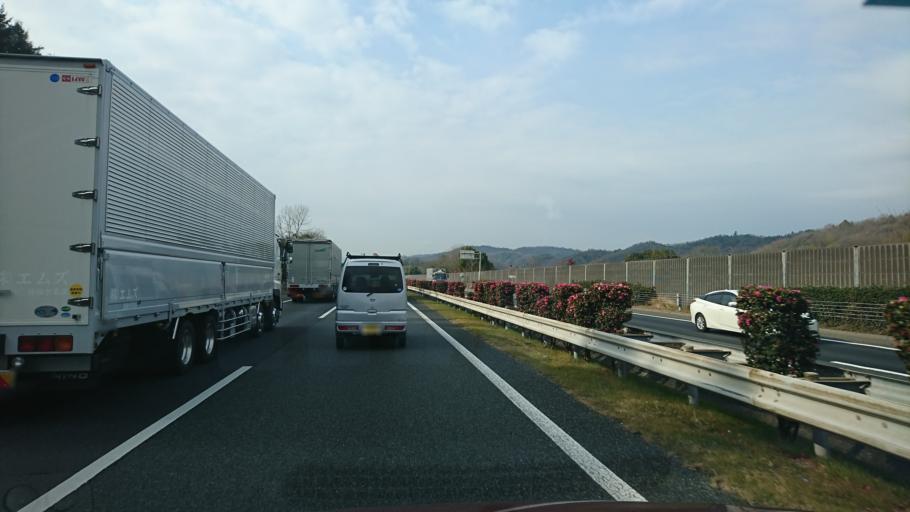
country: JP
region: Hiroshima
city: Kannabecho-yahiro
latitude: 34.5387
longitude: 133.4631
